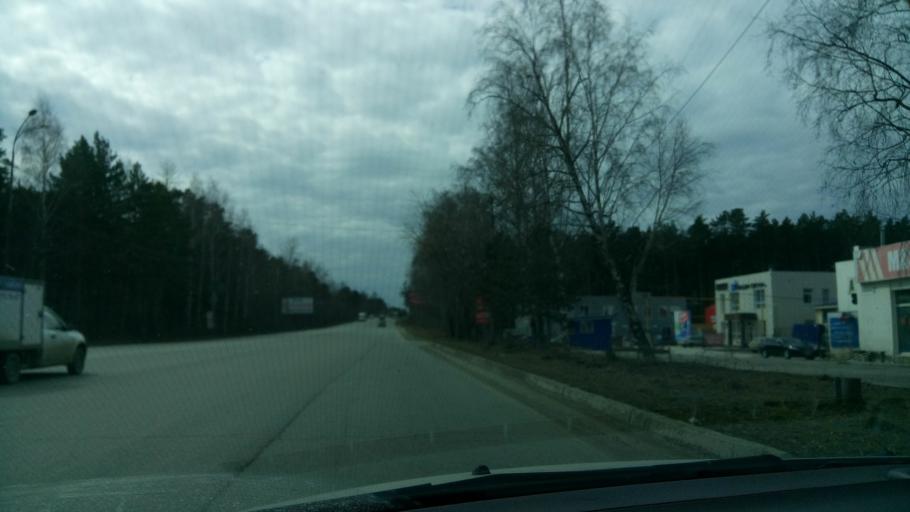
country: RU
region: Sverdlovsk
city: Beryozovsky
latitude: 56.8967
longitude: 60.7611
